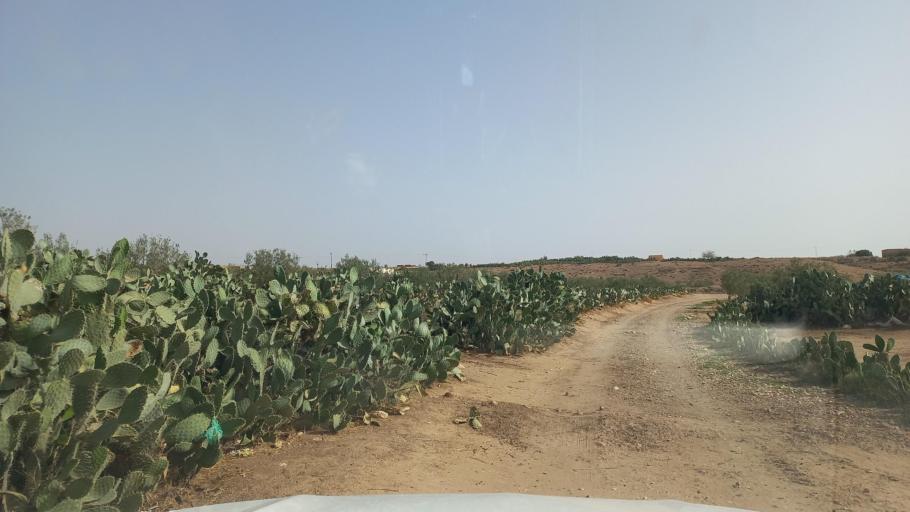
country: TN
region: Al Qasrayn
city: Kasserine
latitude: 35.2992
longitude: 8.9622
